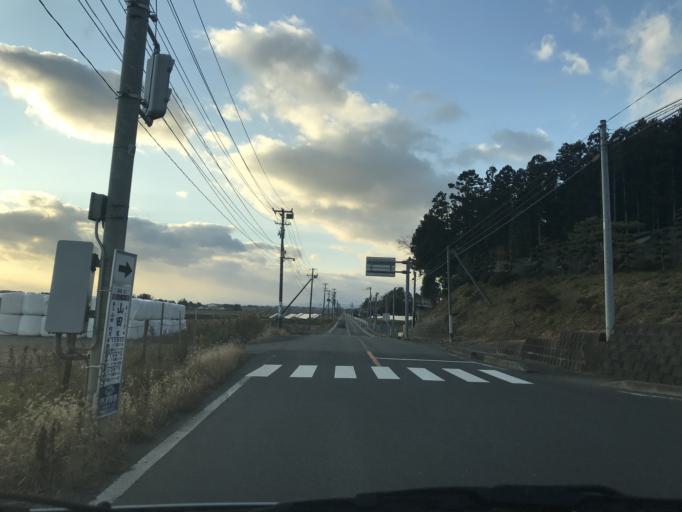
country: JP
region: Miyagi
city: Kogota
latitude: 38.6532
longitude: 141.0576
